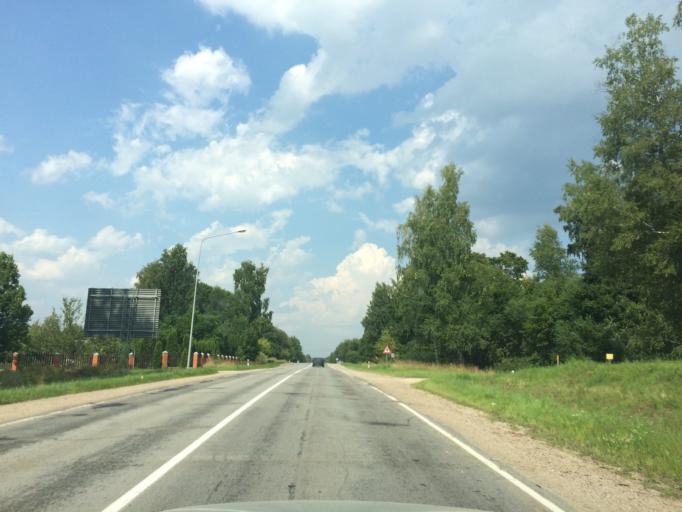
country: LV
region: Rezekne
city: Rezekne
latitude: 56.5473
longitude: 27.3558
